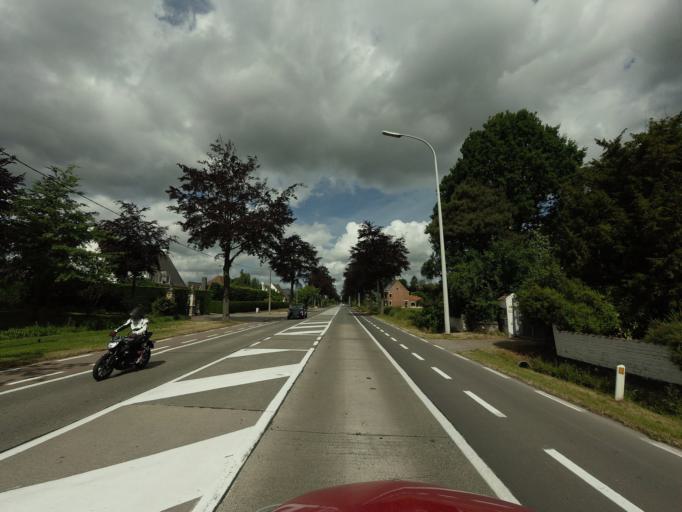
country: BE
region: Flanders
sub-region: Provincie Oost-Vlaanderen
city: Eeklo
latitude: 51.1931
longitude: 3.5479
